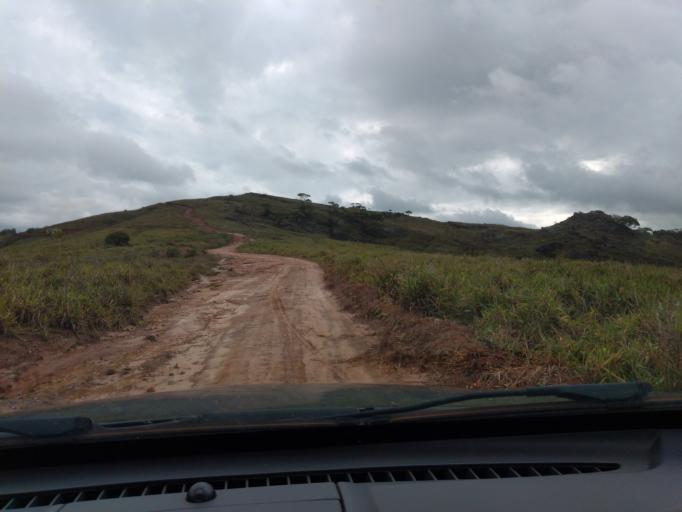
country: BR
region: Minas Gerais
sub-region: Lavras
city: Lavras
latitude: -21.5154
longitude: -44.9297
